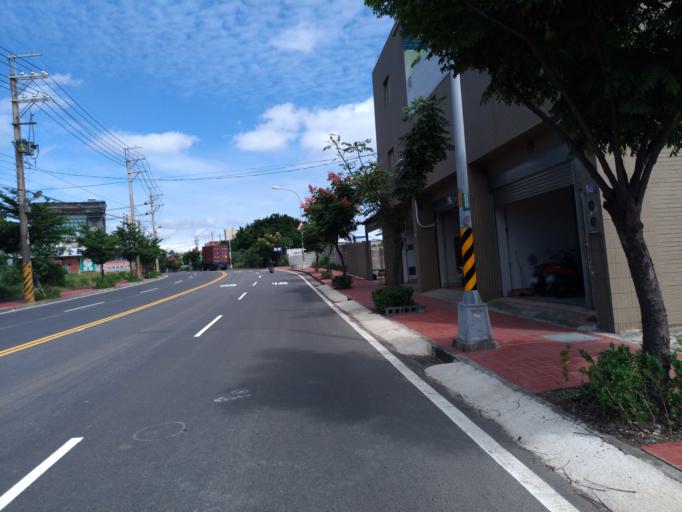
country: TW
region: Taiwan
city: Taoyuan City
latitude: 24.9513
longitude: 121.1663
